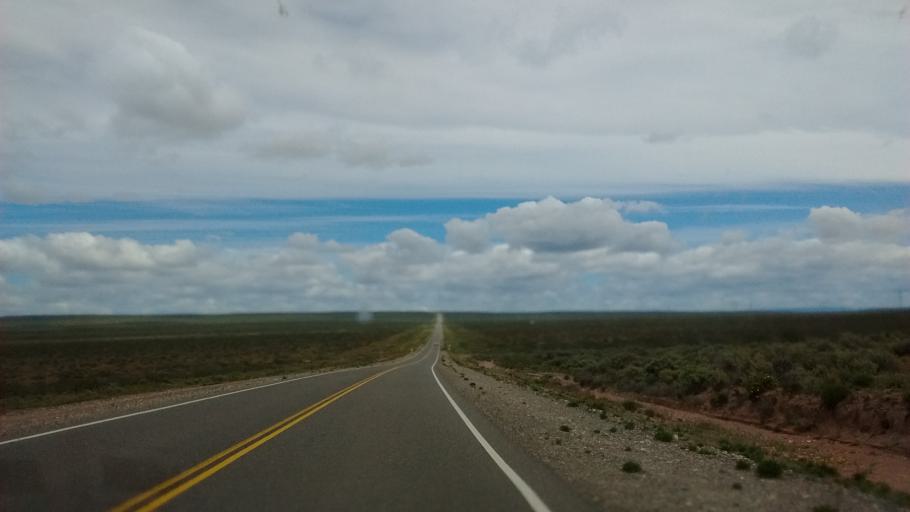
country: AR
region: Neuquen
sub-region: Departamento de Picun Leufu
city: Picun Leufu
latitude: -39.7120
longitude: -69.5148
